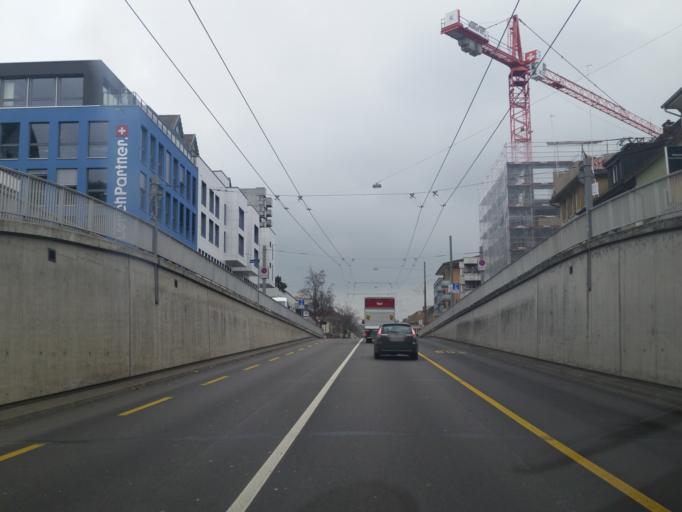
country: CH
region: Zurich
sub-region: Bezirk Winterthur
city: Toess (Kreis 4) / Schlosstal
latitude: 47.4904
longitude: 8.7049
